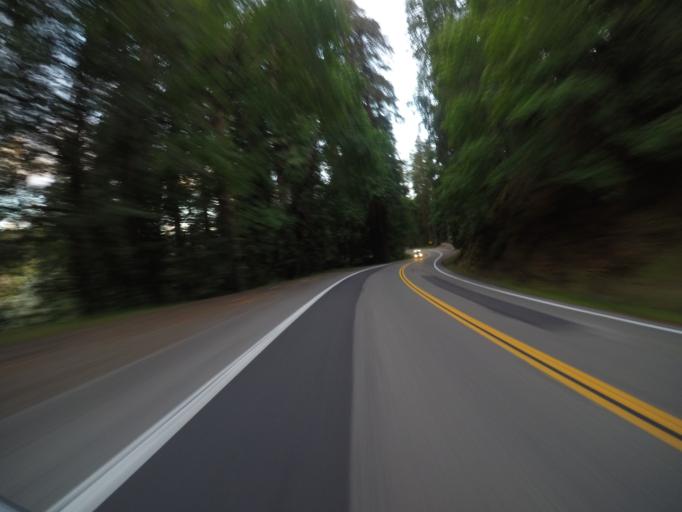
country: US
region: California
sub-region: Humboldt County
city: Redway
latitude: 40.0131
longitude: -123.7909
